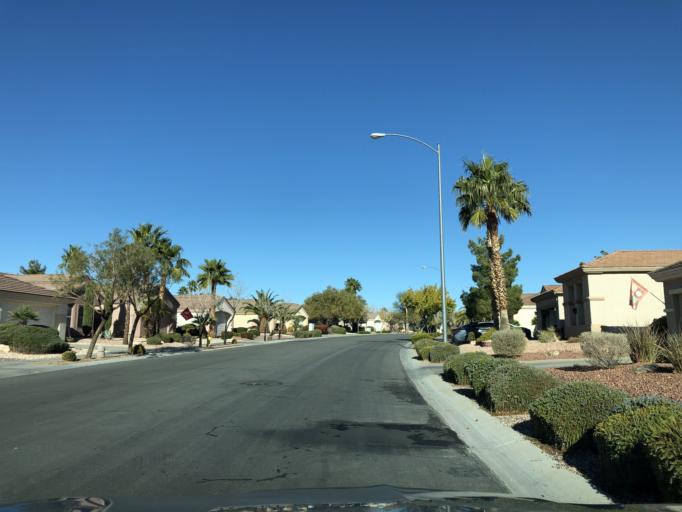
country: US
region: Nevada
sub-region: Clark County
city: Whitney
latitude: 36.0084
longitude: -115.0687
